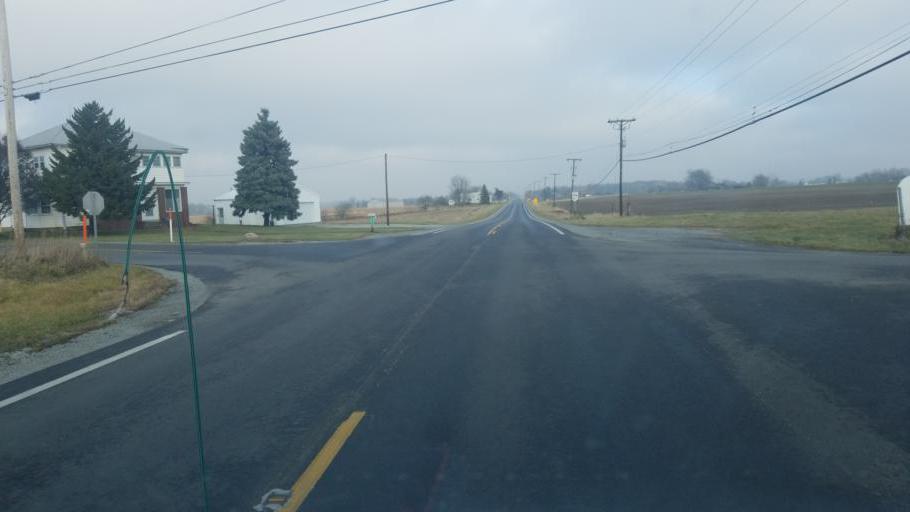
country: US
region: Ohio
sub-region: Hardin County
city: Kenton
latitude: 40.6574
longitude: -83.5764
